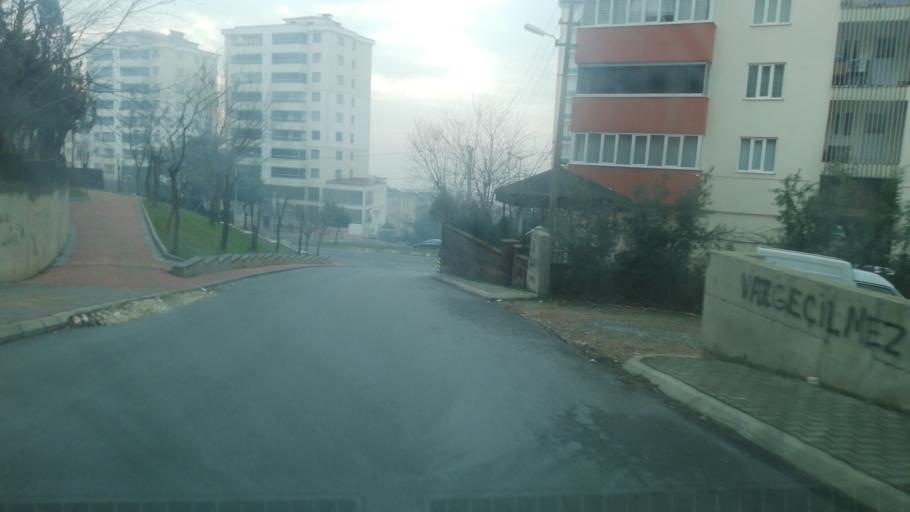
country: TR
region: Kahramanmaras
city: Kahramanmaras
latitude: 37.5934
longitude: 36.9010
